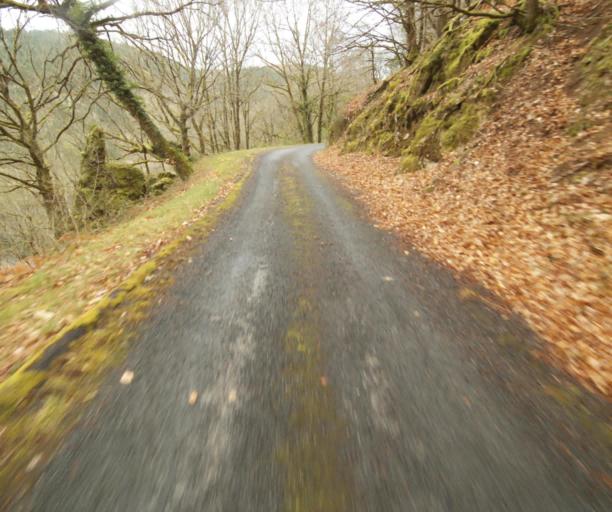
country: FR
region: Limousin
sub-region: Departement de la Correze
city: Saint-Privat
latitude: 45.2104
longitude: 2.0345
